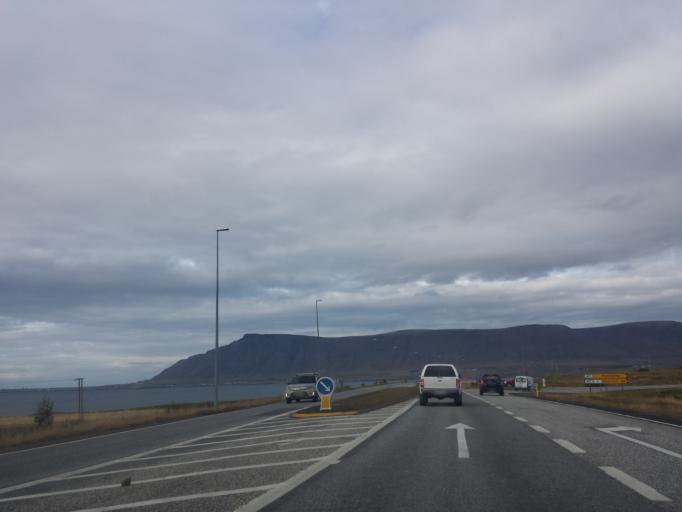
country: IS
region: Capital Region
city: Reykjavik
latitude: 64.2735
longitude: -21.8373
